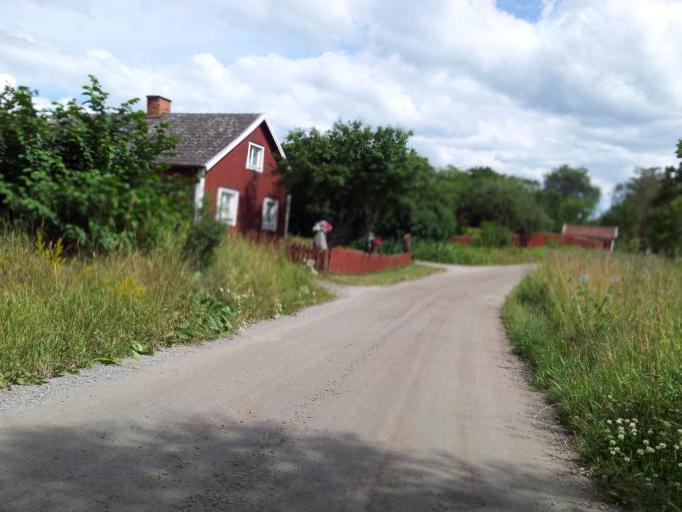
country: SE
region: Stockholm
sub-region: Norrtalje Kommun
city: Nykvarn
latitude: 59.8985
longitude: 18.1990
